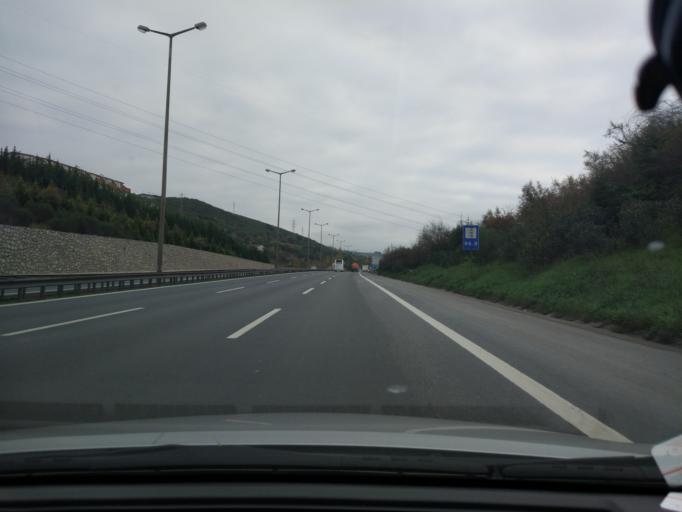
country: TR
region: Kocaeli
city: Izmit
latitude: 40.7701
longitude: 29.8687
